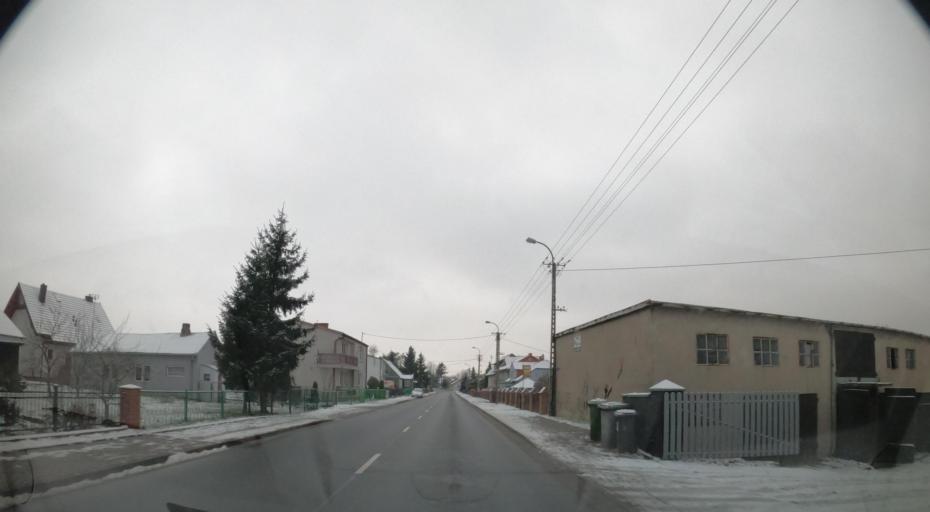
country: PL
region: Kujawsko-Pomorskie
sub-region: Powiat lipnowski
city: Wielgie
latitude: 52.7402
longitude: 19.2673
